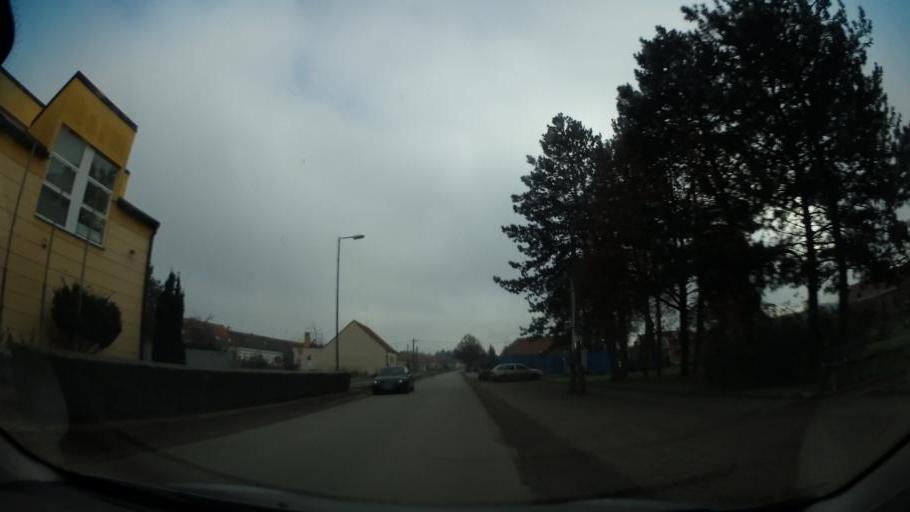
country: CZ
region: Vysocina
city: Mohelno
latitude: 49.1237
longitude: 16.2460
